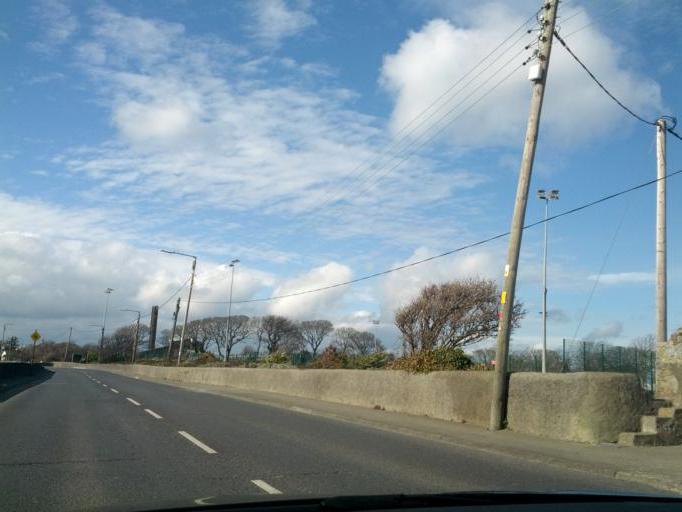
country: IE
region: Leinster
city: Sutton
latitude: 53.3855
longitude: -6.1015
